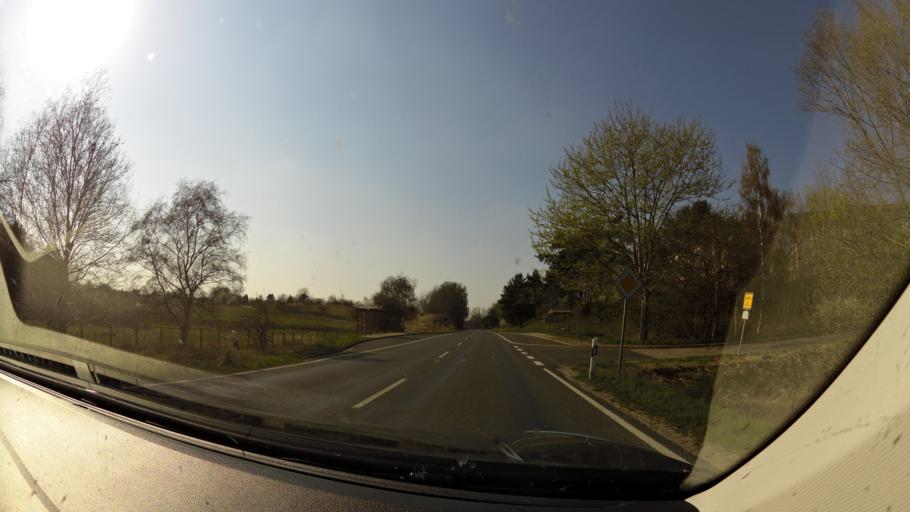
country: DE
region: Mecklenburg-Vorpommern
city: Bad Sulze
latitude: 54.1055
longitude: 12.6625
